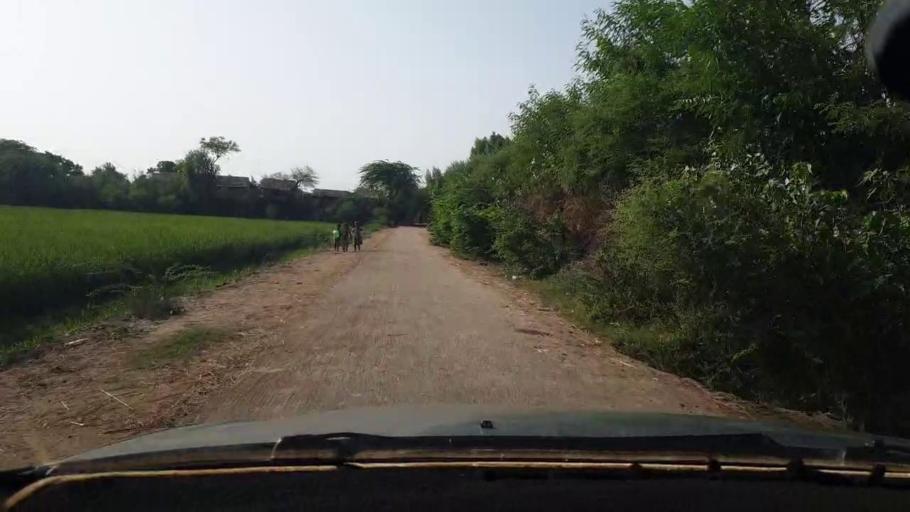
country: PK
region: Sindh
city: Tando Bago
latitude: 24.8187
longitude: 68.8989
